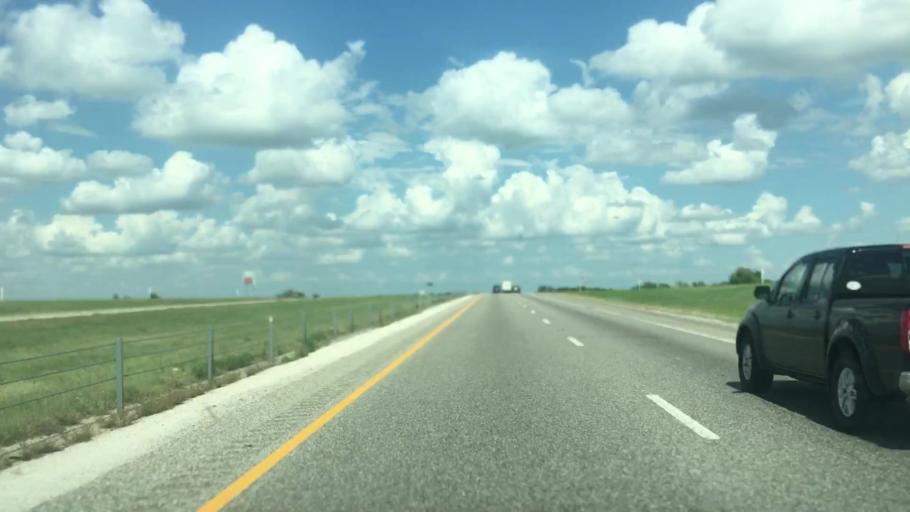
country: US
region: Texas
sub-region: Ellis County
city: Plum Grove
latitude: 32.1054
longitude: -97.0083
